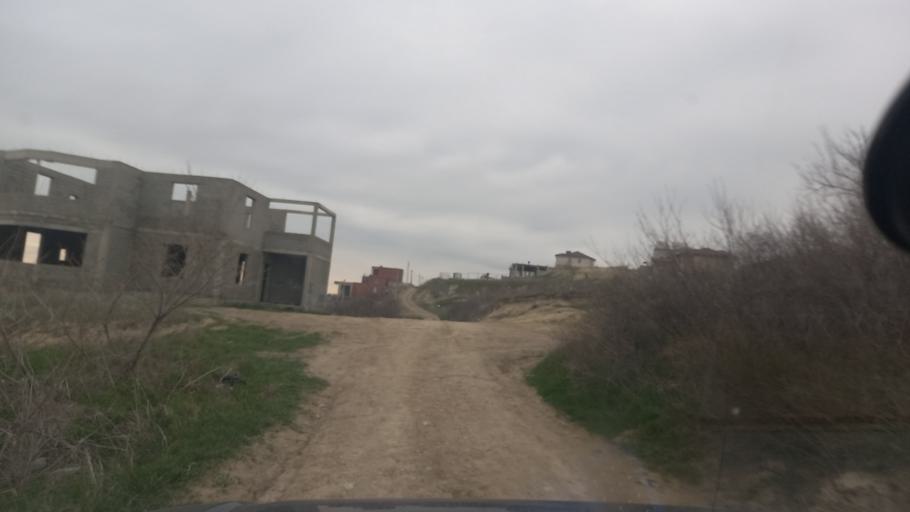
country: RU
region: Krasnodarskiy
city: Anapa
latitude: 44.8535
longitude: 37.3395
